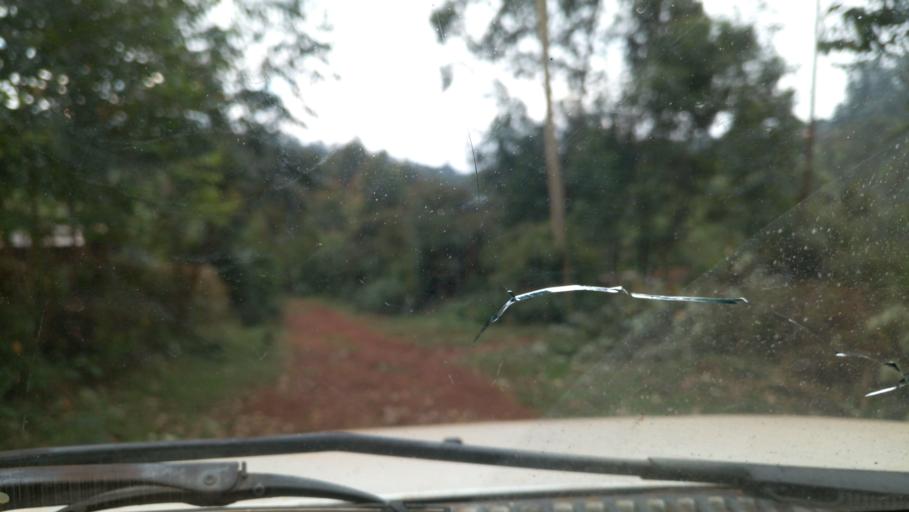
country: KE
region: Murang'a District
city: Kangema
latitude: -0.7672
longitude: 36.8453
